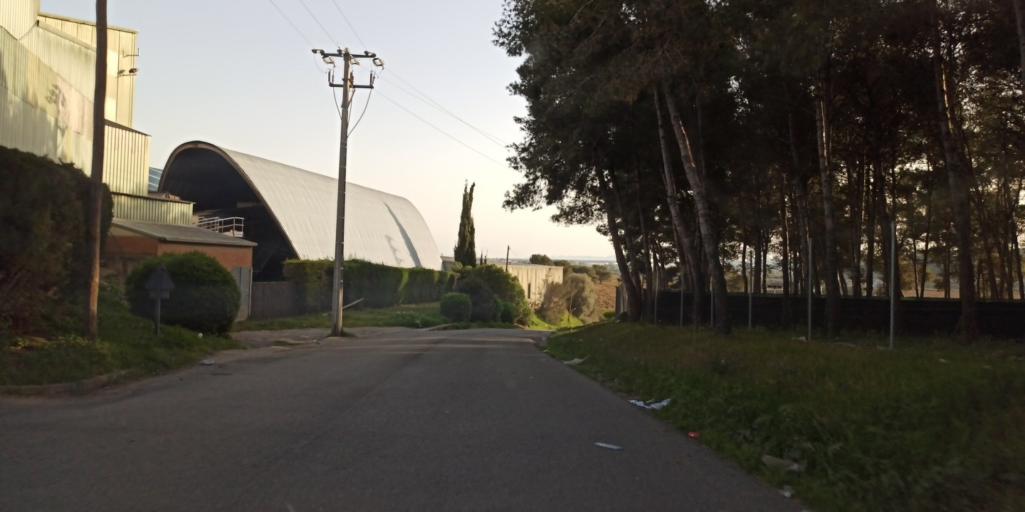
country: ES
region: Catalonia
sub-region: Provincia de Barcelona
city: Vilafranca del Penedes
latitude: 41.3269
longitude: 1.7063
